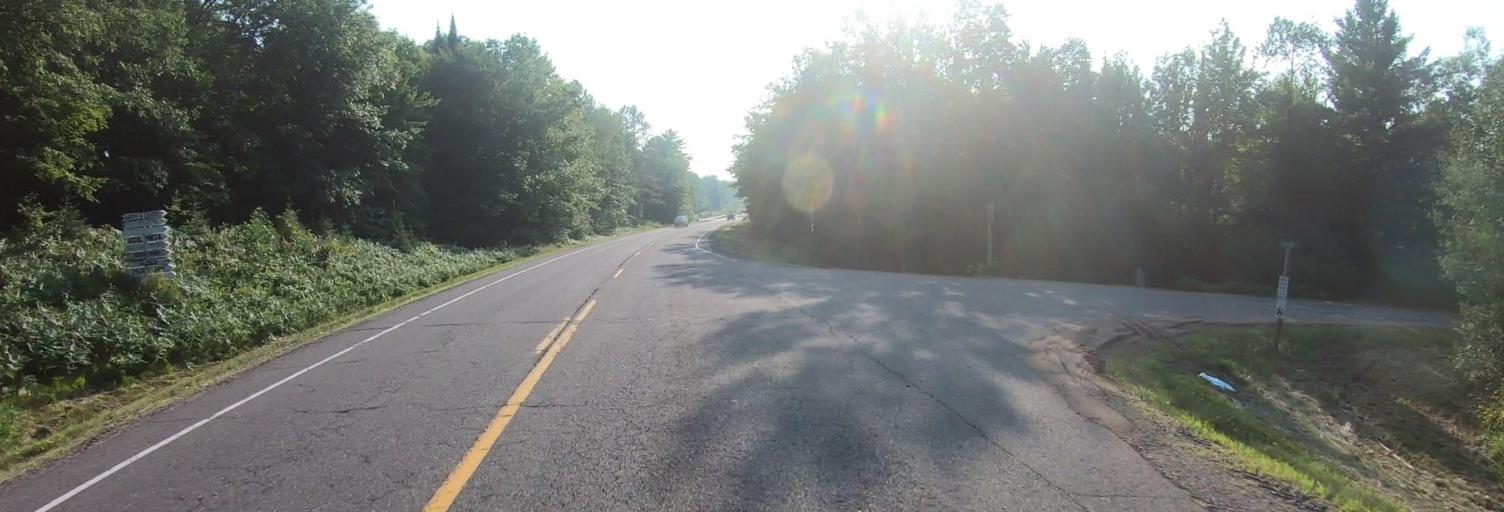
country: US
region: Wisconsin
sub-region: Sawyer County
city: Little Round Lake
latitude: 46.0720
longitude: -91.0904
